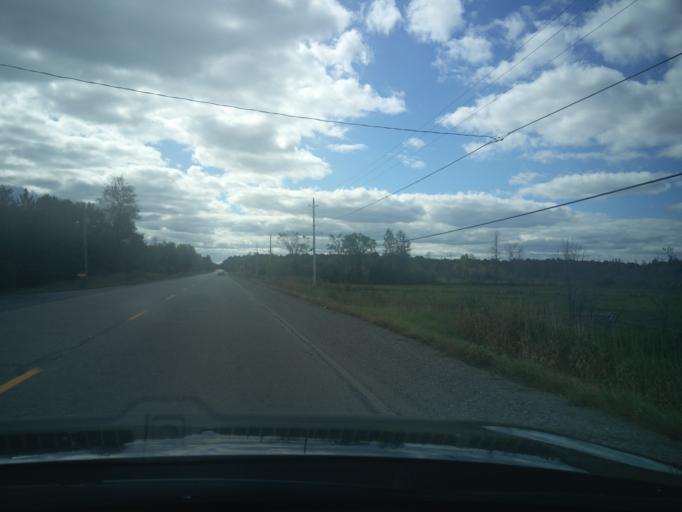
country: CA
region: Ontario
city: Carleton Place
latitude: 45.0550
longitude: -76.0516
